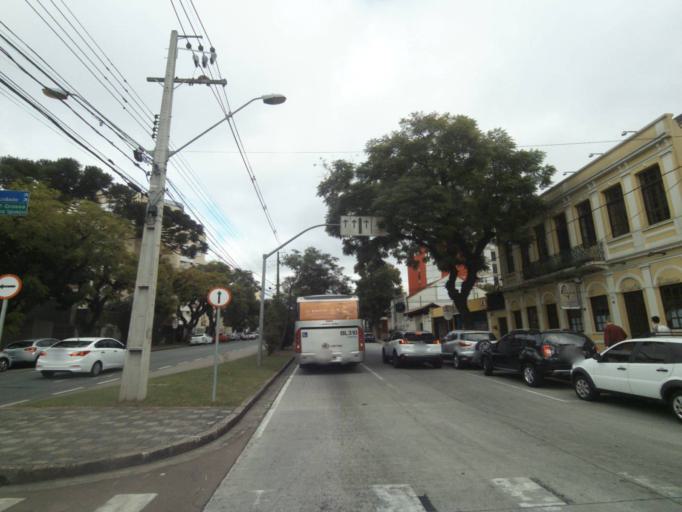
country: BR
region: Parana
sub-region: Curitiba
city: Curitiba
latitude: -25.4438
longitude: -49.2738
